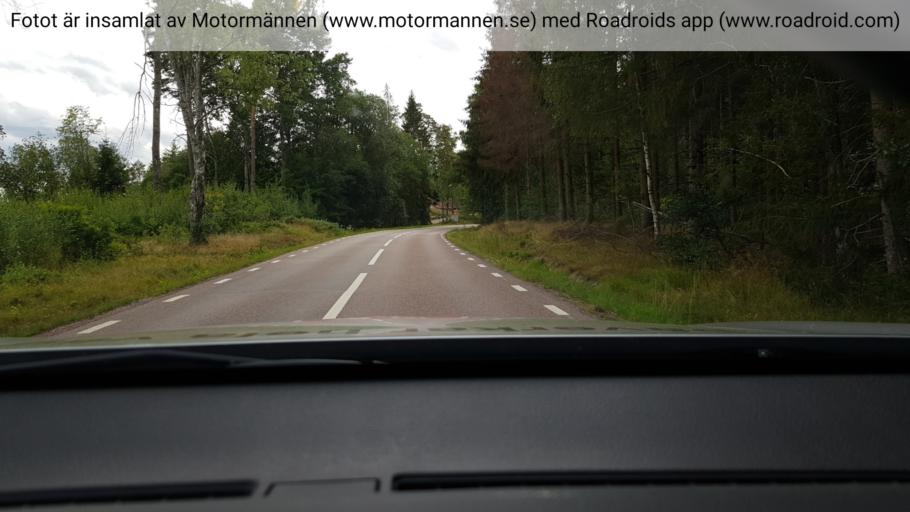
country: SE
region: Soedermanland
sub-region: Nykopings Kommun
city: Nykoping
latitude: 58.9312
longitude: 17.1086
